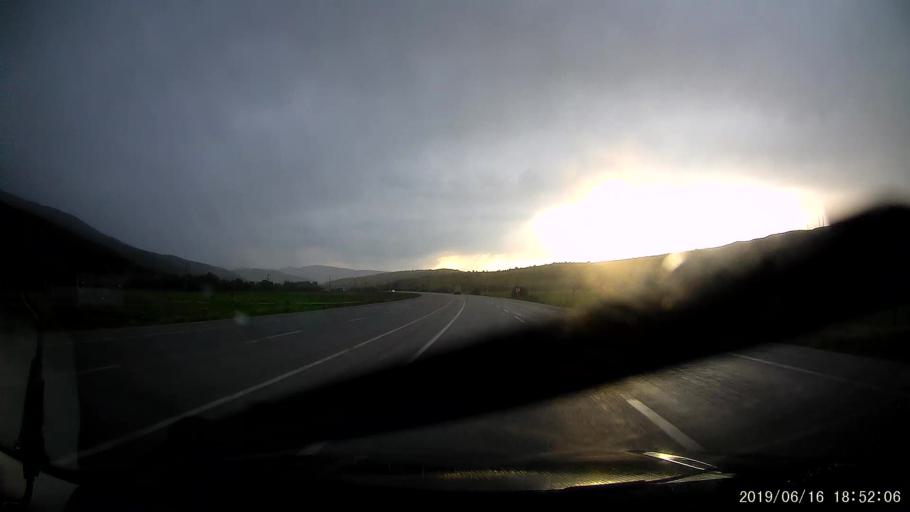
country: TR
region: Erzincan
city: Catalcam
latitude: 39.9030
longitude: 38.9104
